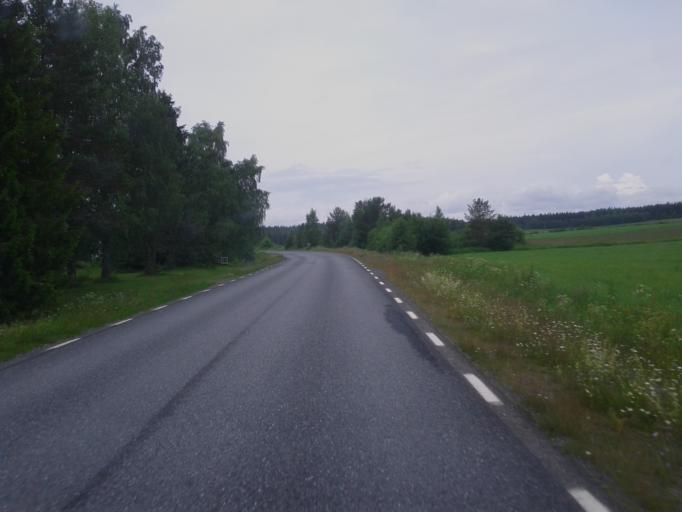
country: SE
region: Vaesterbotten
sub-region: Skelleftea Kommun
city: Forsbacka
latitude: 64.8980
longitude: 20.6833
